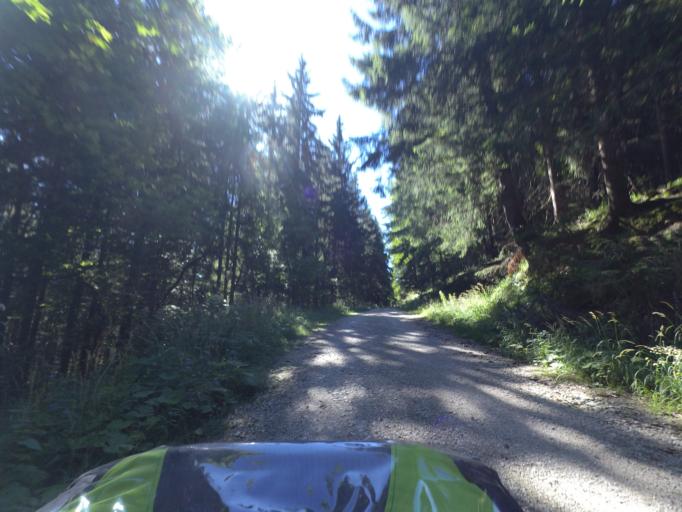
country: AT
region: Salzburg
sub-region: Politischer Bezirk Hallein
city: Hallein
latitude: 47.6444
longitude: 13.0983
